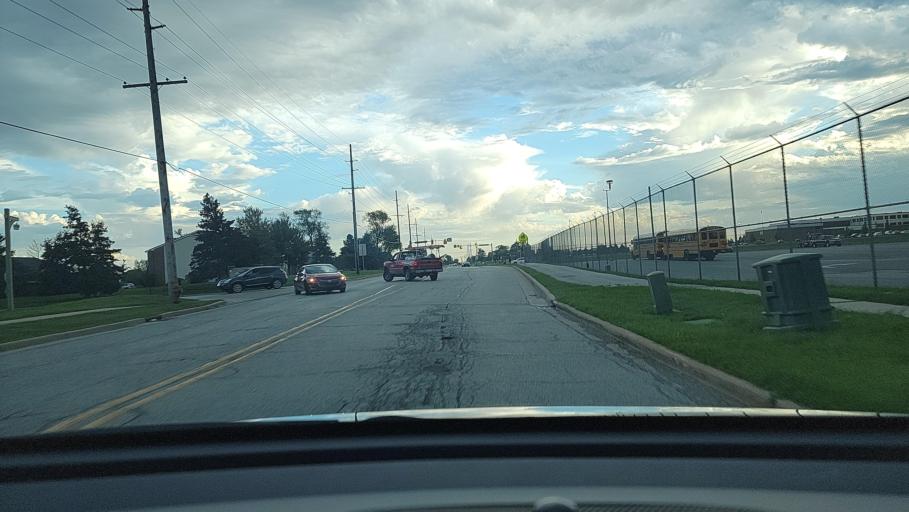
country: US
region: Indiana
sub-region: Porter County
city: Portage
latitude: 41.5558
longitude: -87.1634
